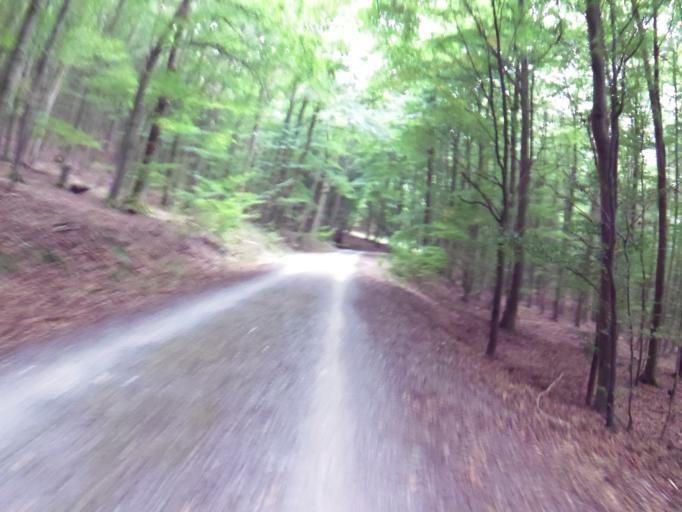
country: DE
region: North Rhine-Westphalia
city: Heimbach
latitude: 50.6243
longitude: 6.4117
